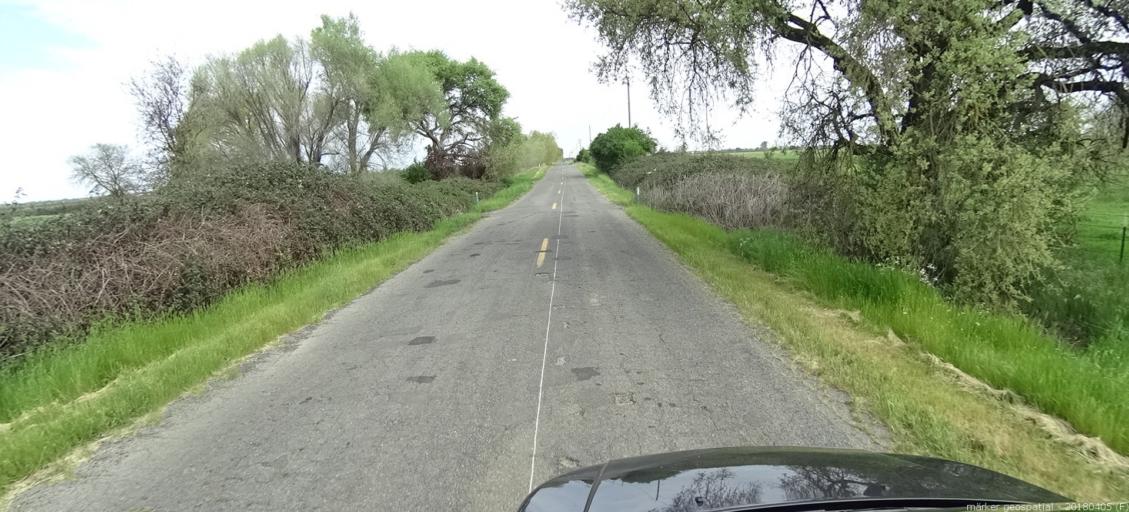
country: US
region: California
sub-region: San Joaquin County
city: Thornton
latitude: 38.2494
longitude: -121.3693
